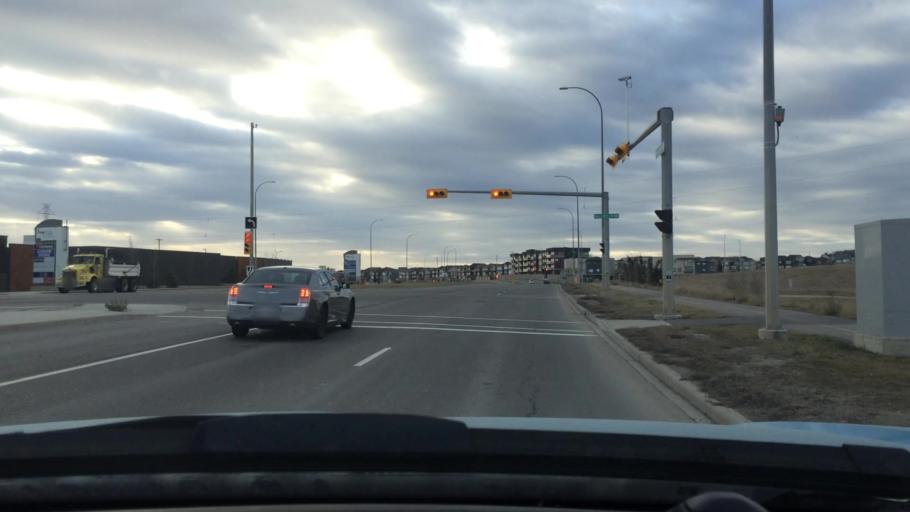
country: CA
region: Alberta
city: Calgary
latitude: 51.1707
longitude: -114.1533
